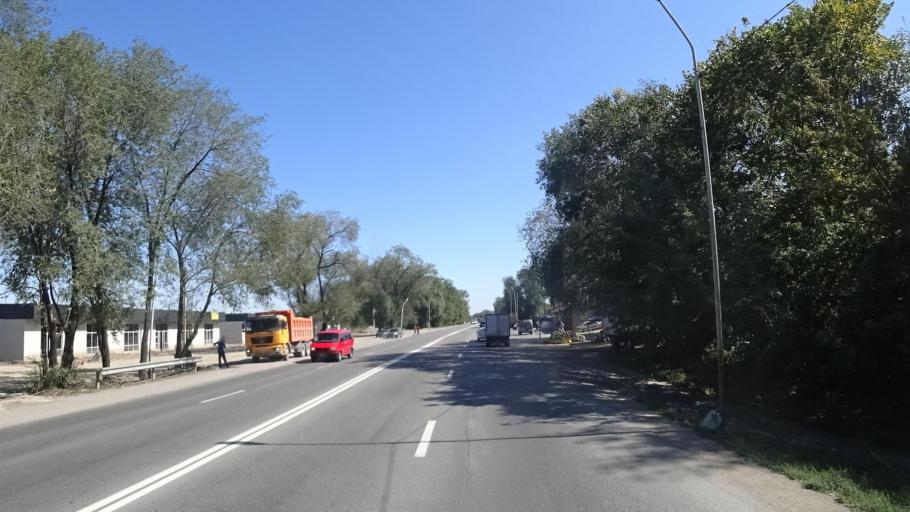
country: KZ
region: Almaty Oblysy
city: Talghar
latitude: 43.4014
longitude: 77.1817
